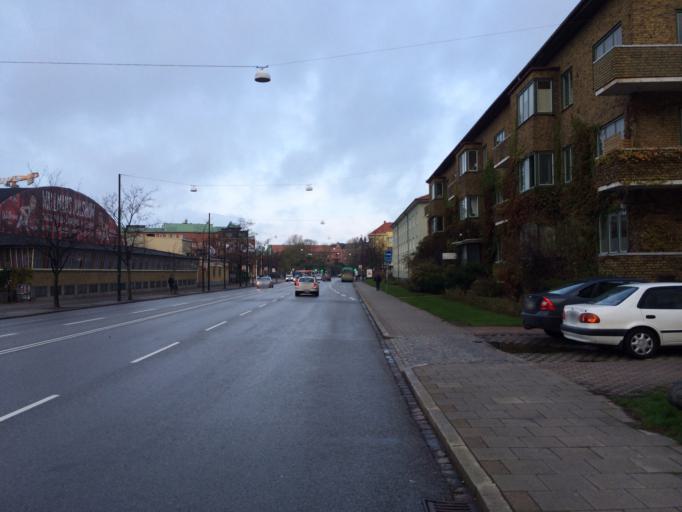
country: SE
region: Skane
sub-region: Malmo
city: Malmoe
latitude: 55.5947
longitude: 13.0157
